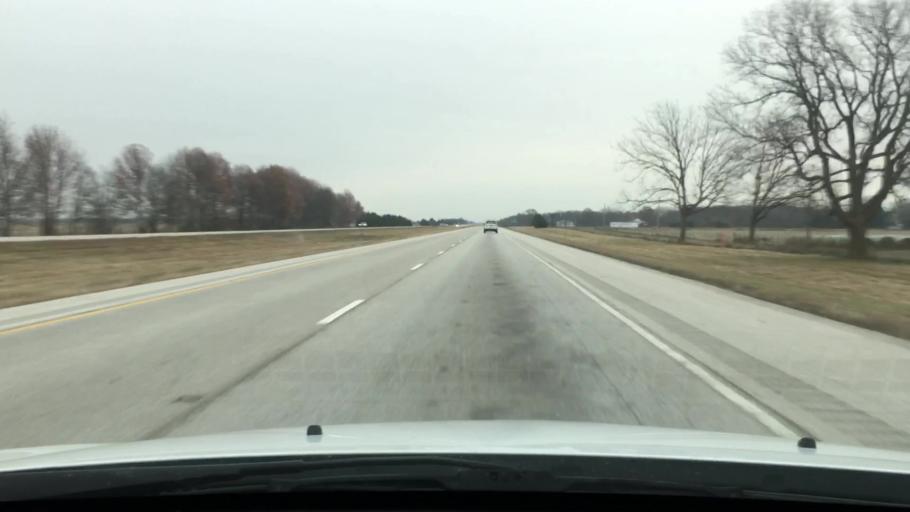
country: US
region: Illinois
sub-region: Morgan County
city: South Jacksonville
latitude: 39.6802
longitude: -90.3203
